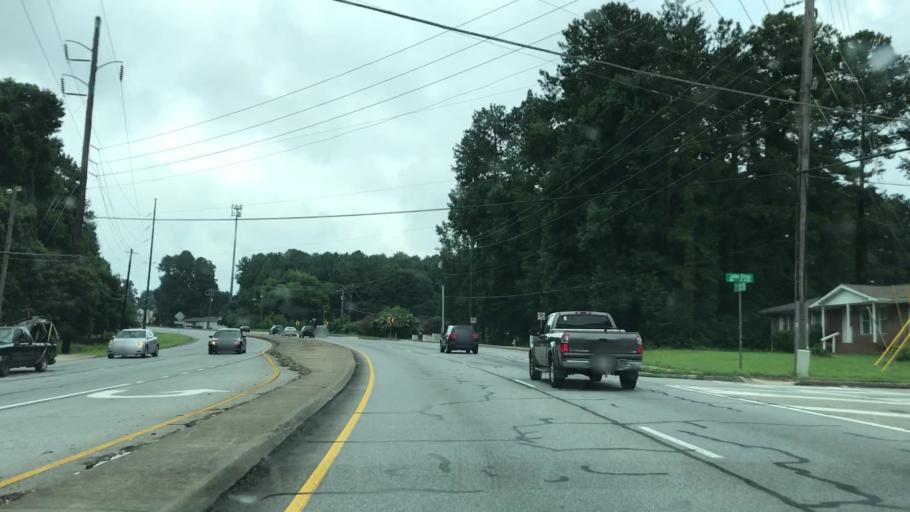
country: US
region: Georgia
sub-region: Gwinnett County
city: Lilburn
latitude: 33.9157
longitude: -84.1371
